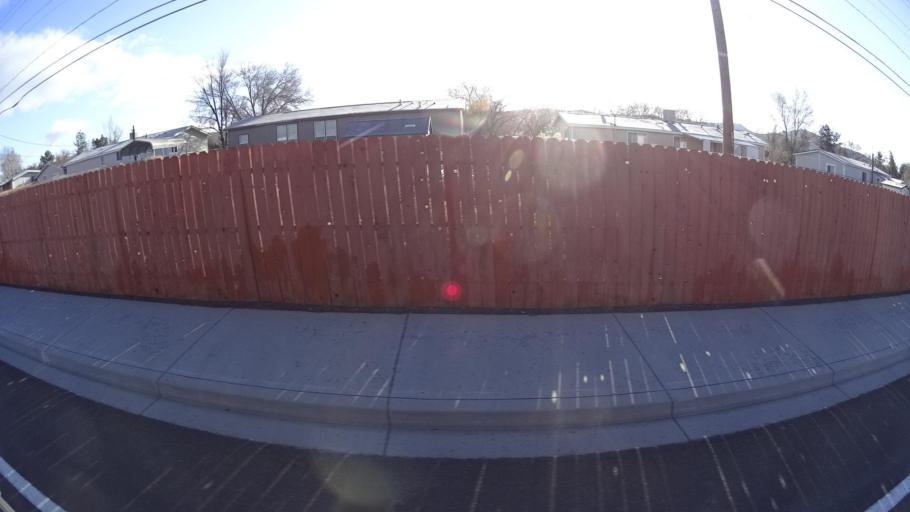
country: US
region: Nevada
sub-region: Washoe County
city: Cold Springs
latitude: 39.6806
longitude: -119.9786
